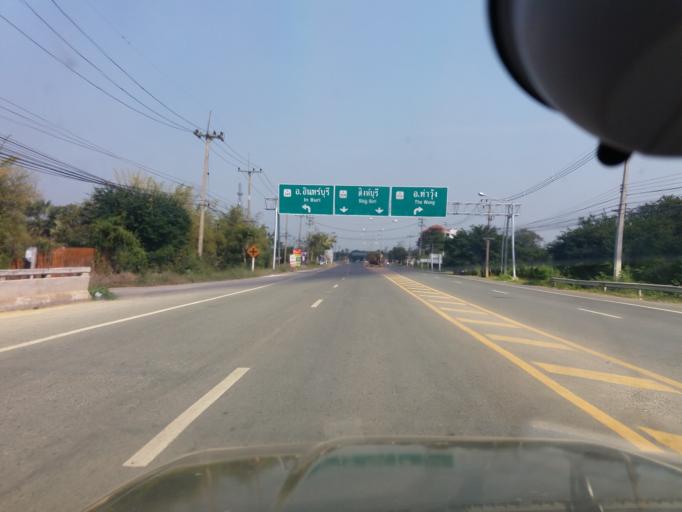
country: TH
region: Sing Buri
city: Sing Buri
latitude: 14.8854
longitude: 100.3880
